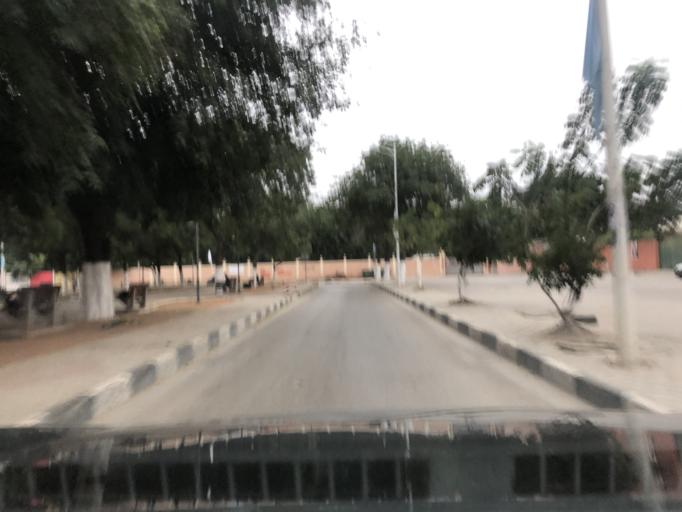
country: AO
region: Luanda
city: Luanda
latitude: -8.8302
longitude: 13.2564
